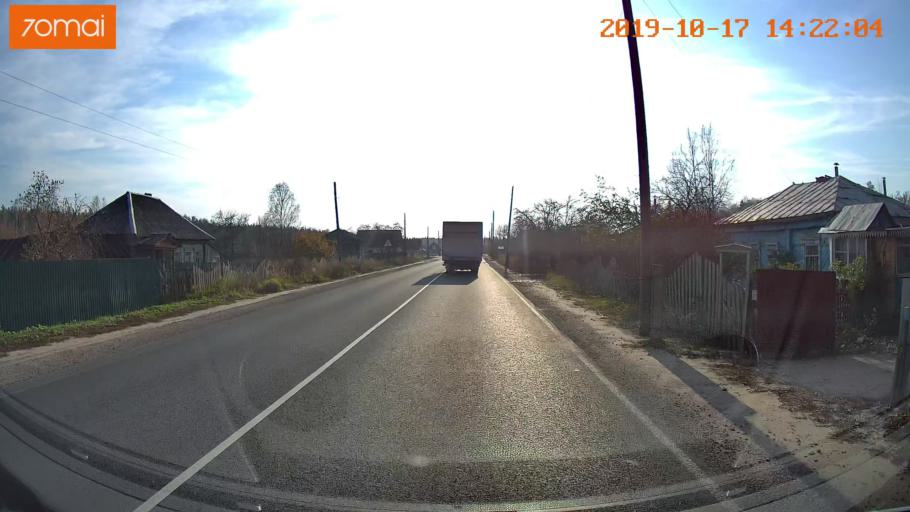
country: RU
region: Moskovskaya
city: Radovitskiy
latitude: 55.0330
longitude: 39.9712
